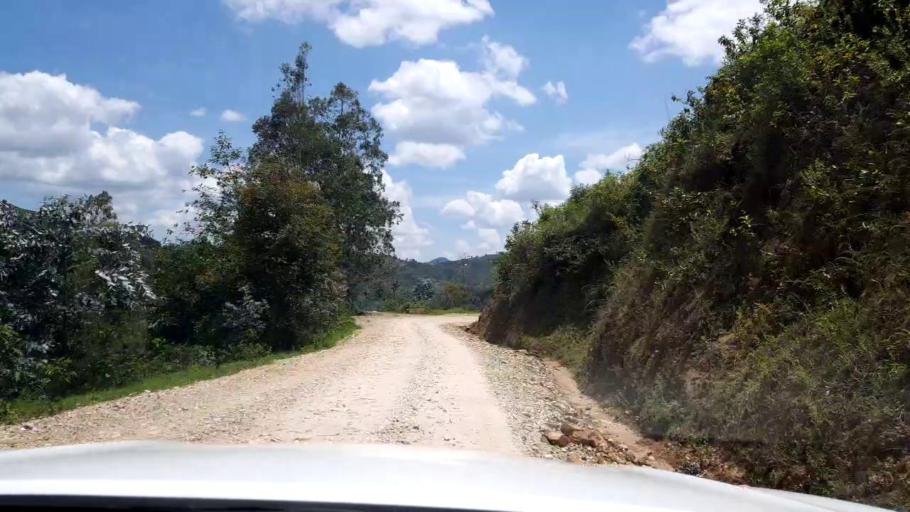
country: RW
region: Southern Province
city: Gitarama
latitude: -1.9838
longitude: 29.6220
